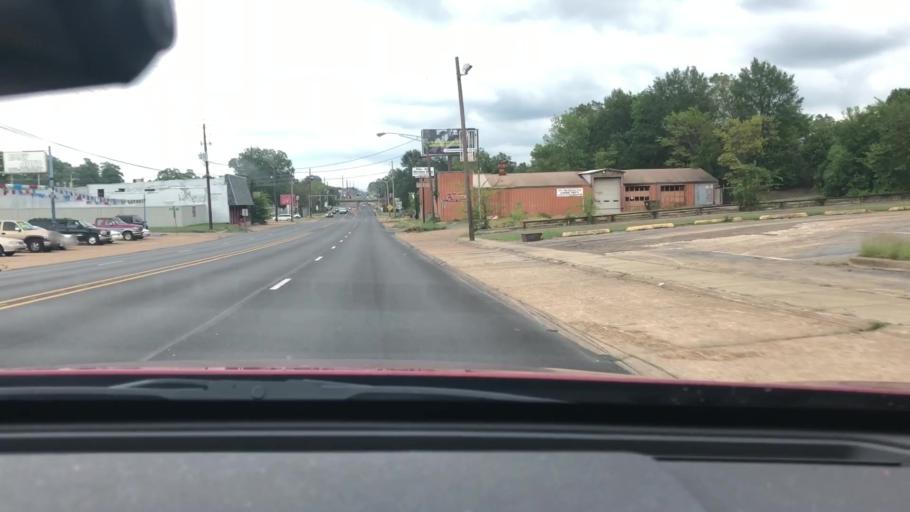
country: US
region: Arkansas
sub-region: Miller County
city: Texarkana
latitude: 33.4308
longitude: -94.0324
